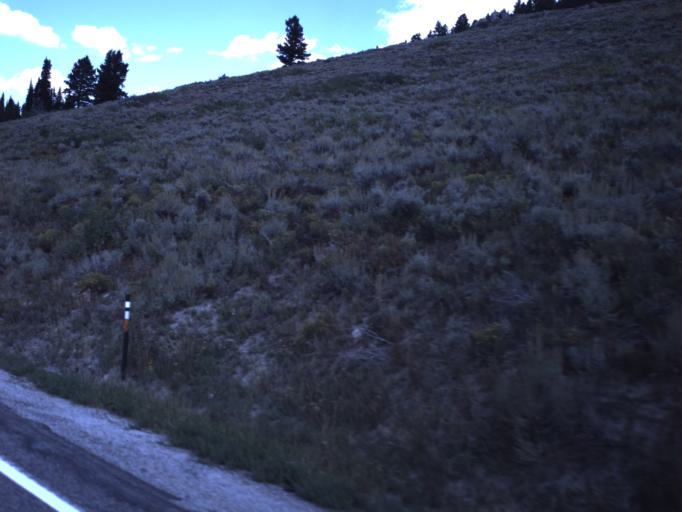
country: US
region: Idaho
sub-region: Bear Lake County
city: Paris
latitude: 41.9312
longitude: -111.4797
